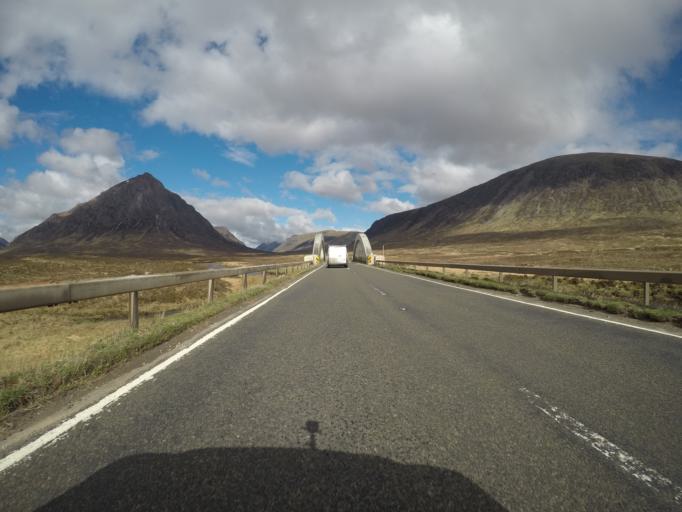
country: GB
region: Scotland
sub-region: Highland
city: Spean Bridge
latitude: 56.6514
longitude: -4.8516
